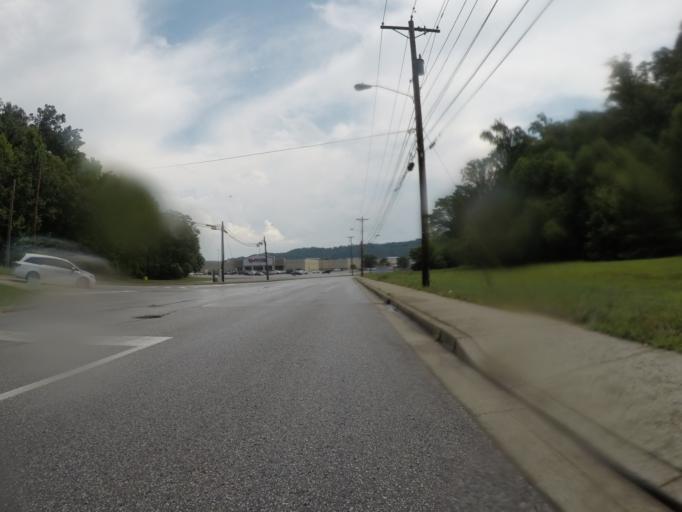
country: US
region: Kentucky
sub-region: Boyd County
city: Westwood
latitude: 38.4812
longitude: -82.6556
